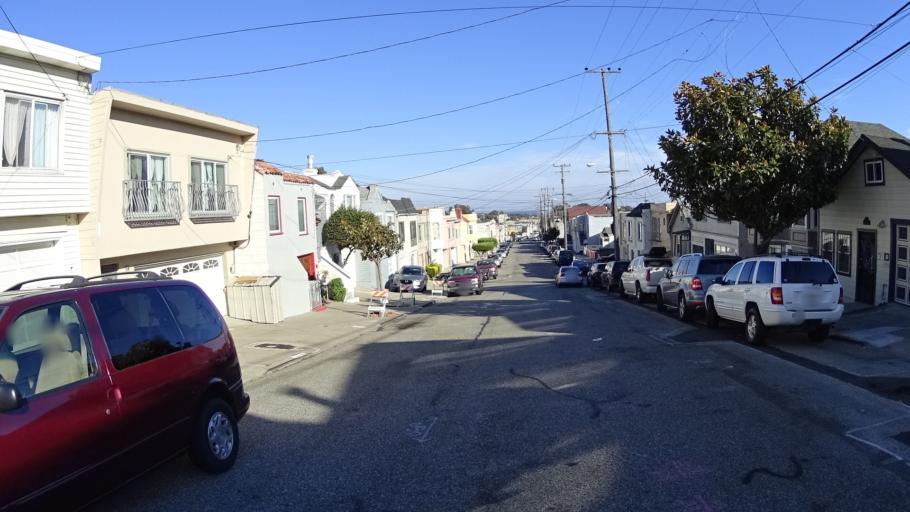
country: US
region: California
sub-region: San Mateo County
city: Brisbane
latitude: 37.7137
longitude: -122.4089
